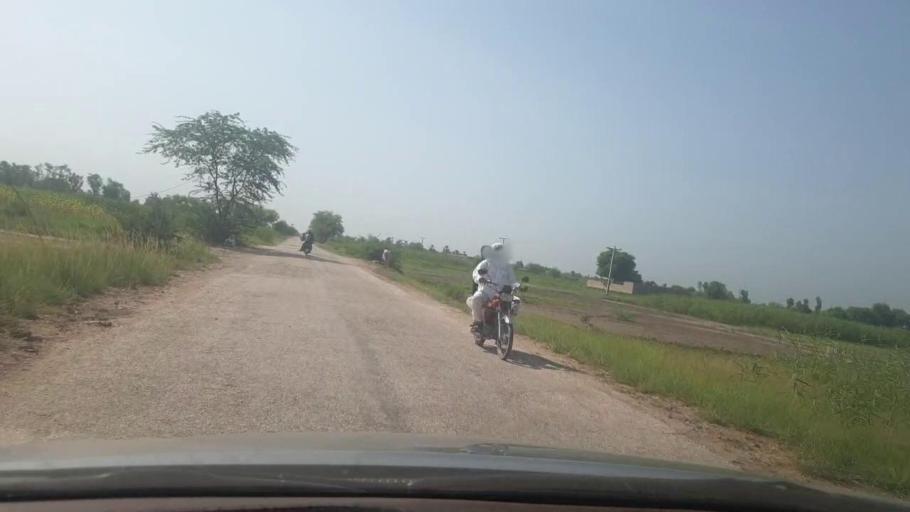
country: PK
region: Sindh
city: Gambat
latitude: 27.3133
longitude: 68.5607
